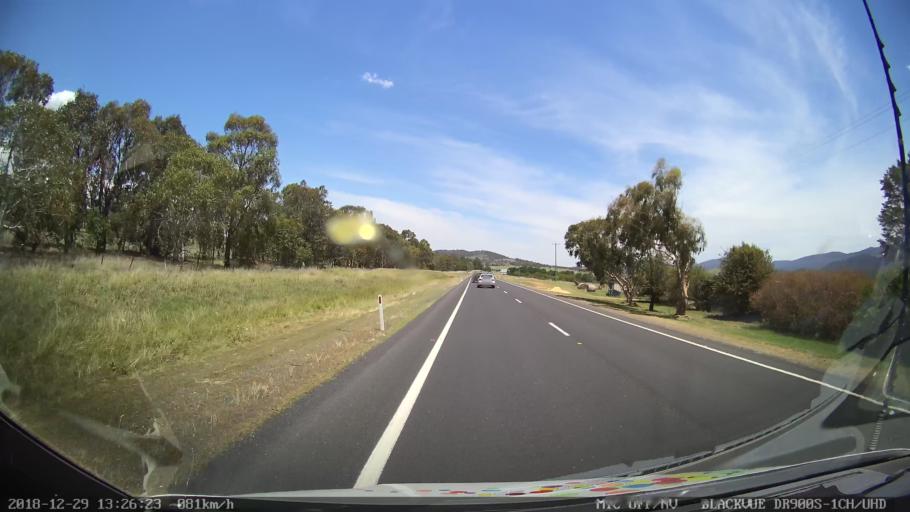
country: AU
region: New South Wales
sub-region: Cooma-Monaro
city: Cooma
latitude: -35.8549
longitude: 149.1592
